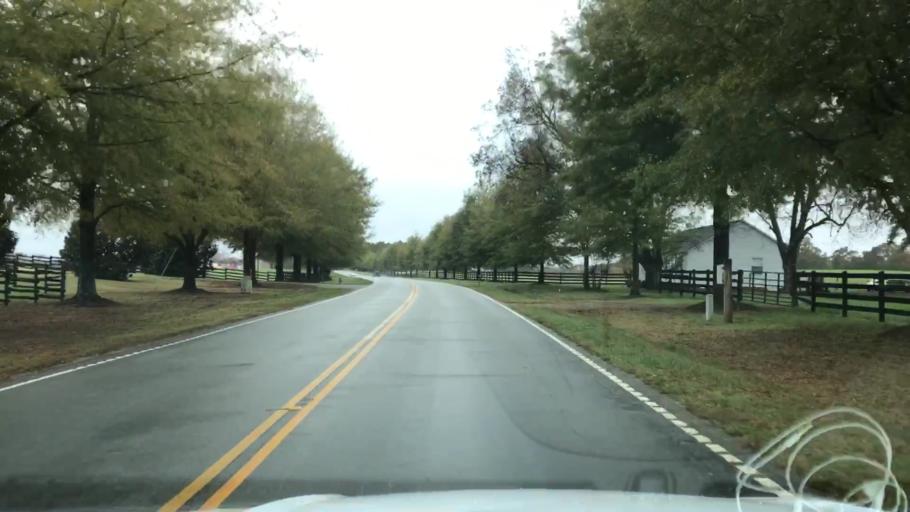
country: US
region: South Carolina
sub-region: Spartanburg County
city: Roebuck
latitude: 34.8093
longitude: -81.9201
